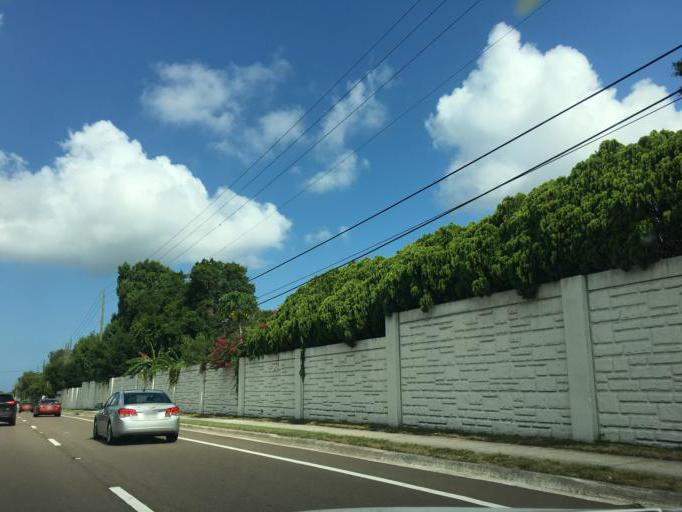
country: US
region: Florida
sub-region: Pinellas County
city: Saint George
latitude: 28.0481
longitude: -82.7498
